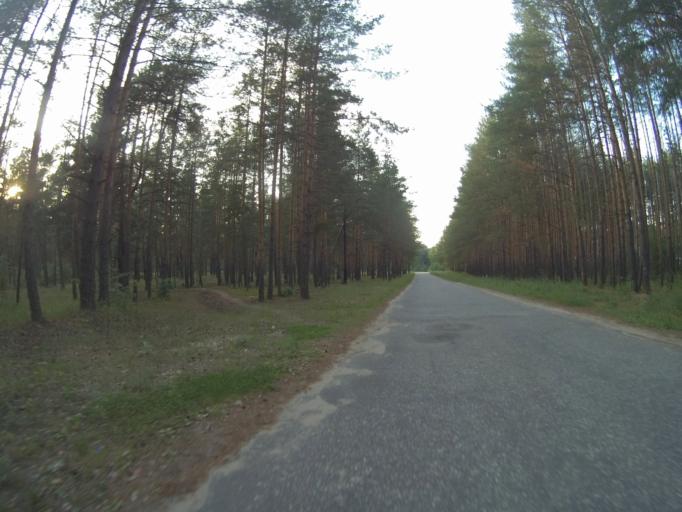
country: RU
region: Vladimir
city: Kommunar
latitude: 56.0857
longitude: 40.4381
